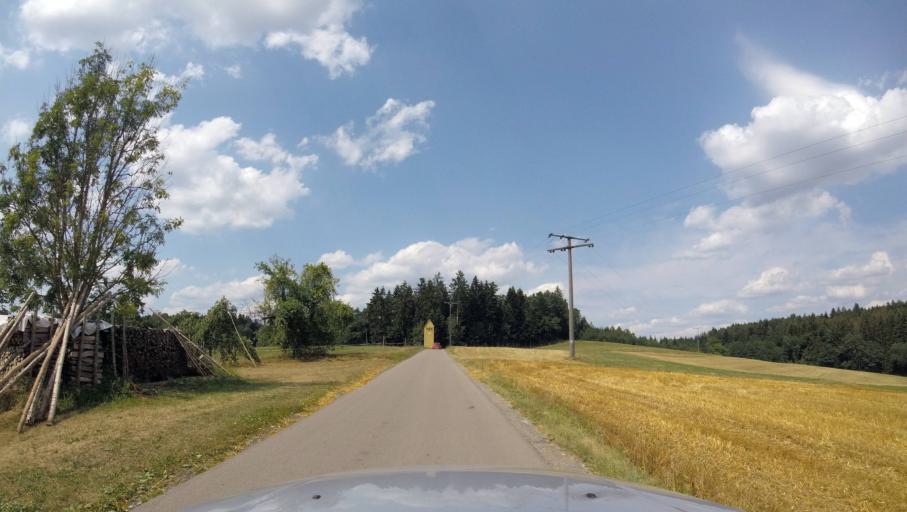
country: DE
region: Baden-Wuerttemberg
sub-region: Regierungsbezirk Stuttgart
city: Spraitbach
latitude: 48.8658
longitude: 9.7482
